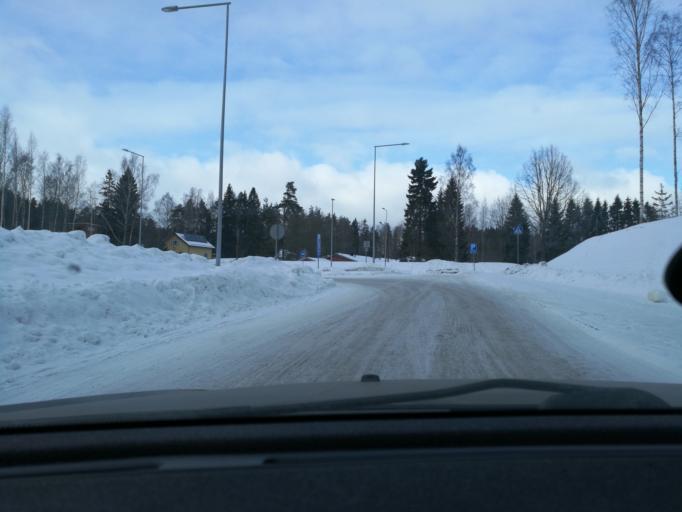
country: FI
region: Uusimaa
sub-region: Helsinki
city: Vantaa
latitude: 60.2830
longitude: 25.0948
